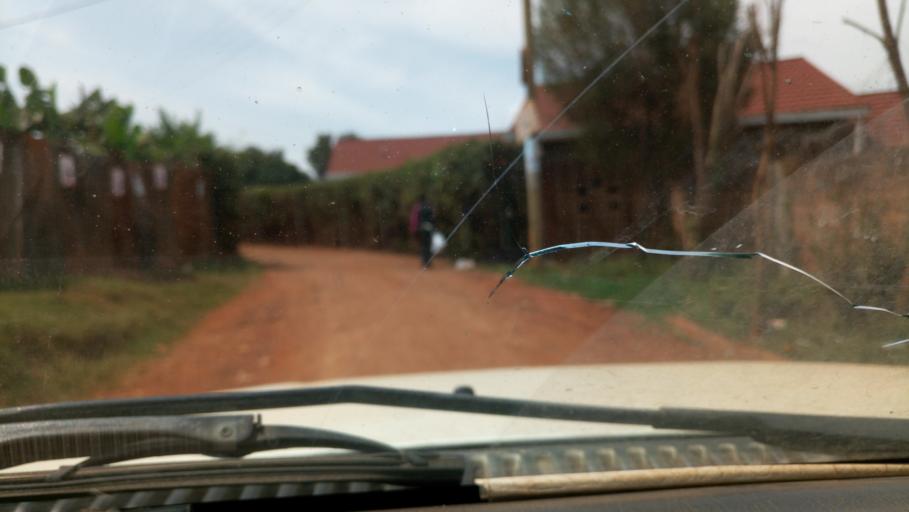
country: KE
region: Kiambu
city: Kikuyu
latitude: -1.2725
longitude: 36.7367
